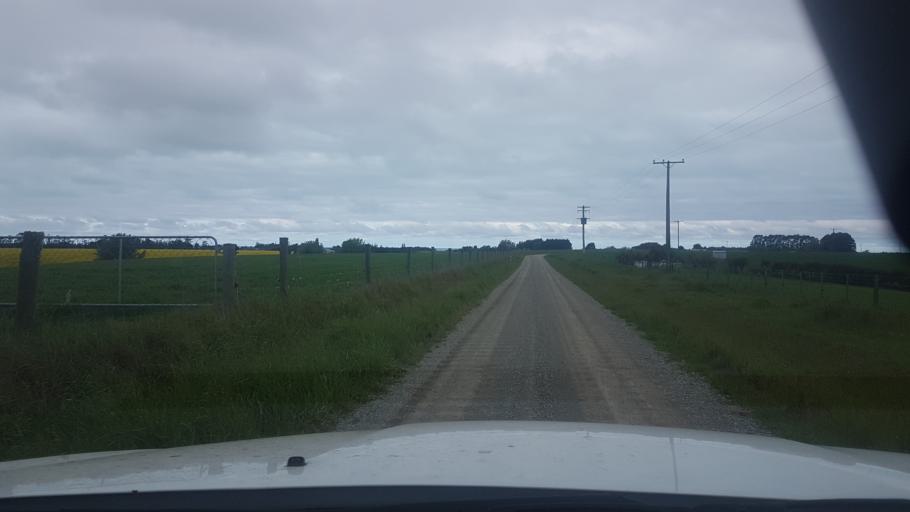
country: NZ
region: Canterbury
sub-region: Timaru District
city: Timaru
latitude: -44.4431
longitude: 171.2032
